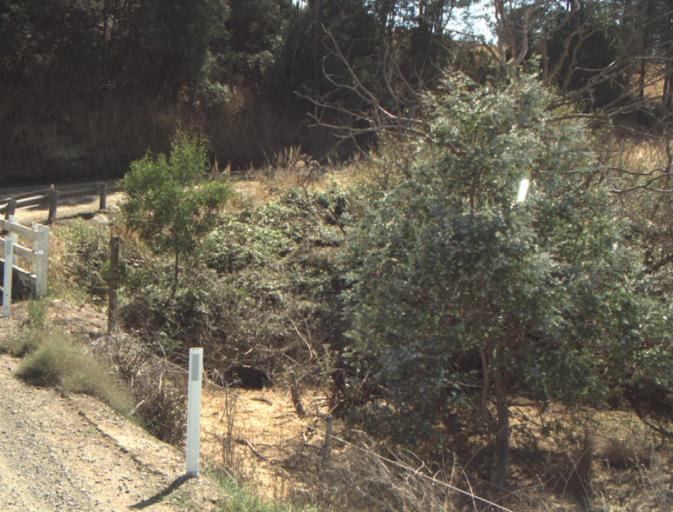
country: AU
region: Tasmania
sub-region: Launceston
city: Mayfield
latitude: -41.2234
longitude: 147.2372
